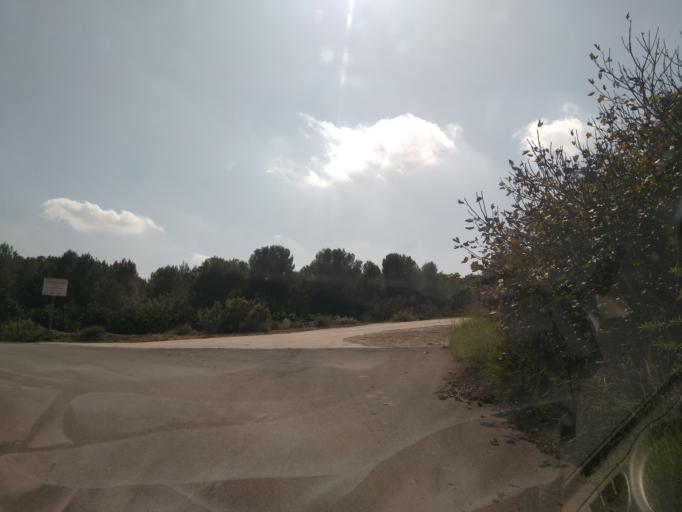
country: ES
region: Valencia
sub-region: Provincia de Valencia
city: Tous
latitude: 39.1790
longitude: -0.6017
